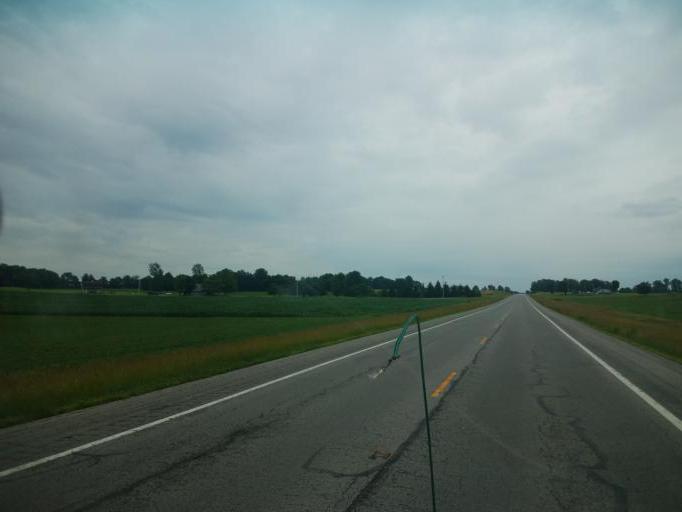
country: US
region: Ohio
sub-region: Hardin County
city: Ada
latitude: 40.7080
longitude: -83.7433
